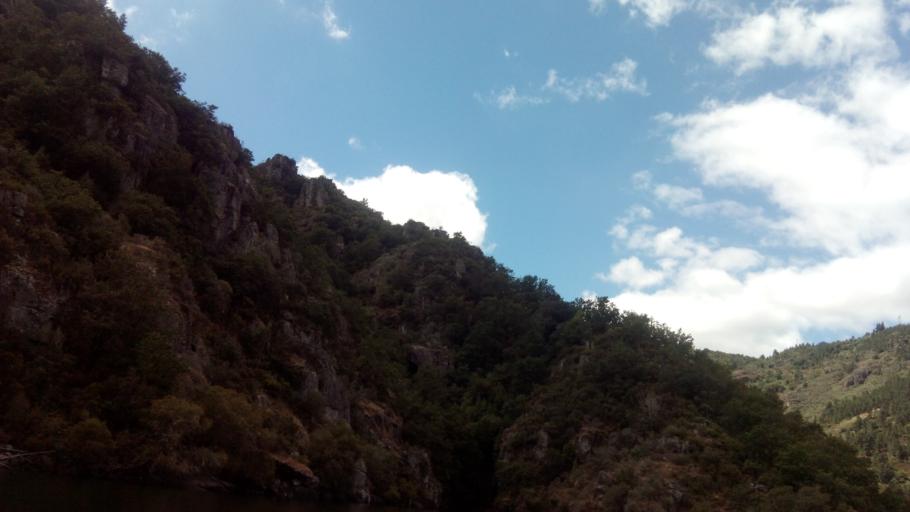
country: ES
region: Galicia
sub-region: Provincia de Lugo
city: Sober
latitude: 42.4071
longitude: -7.6342
